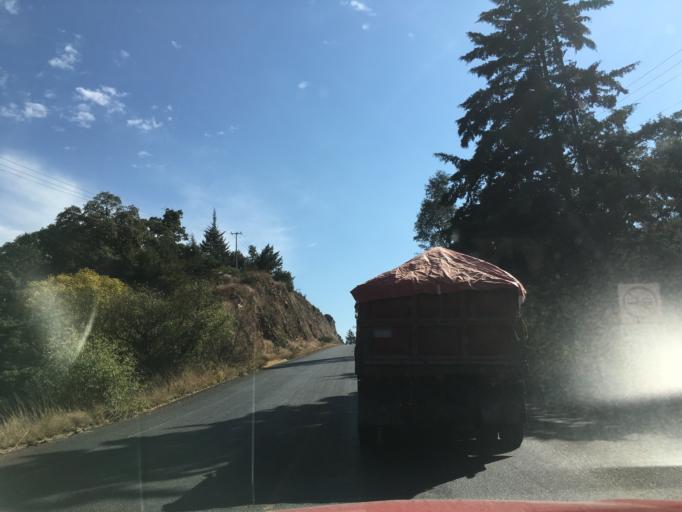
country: MX
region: Michoacan
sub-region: Hidalgo
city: Rincon de Cedenos (Rincon de Dolores)
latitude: 19.6988
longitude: -100.5845
